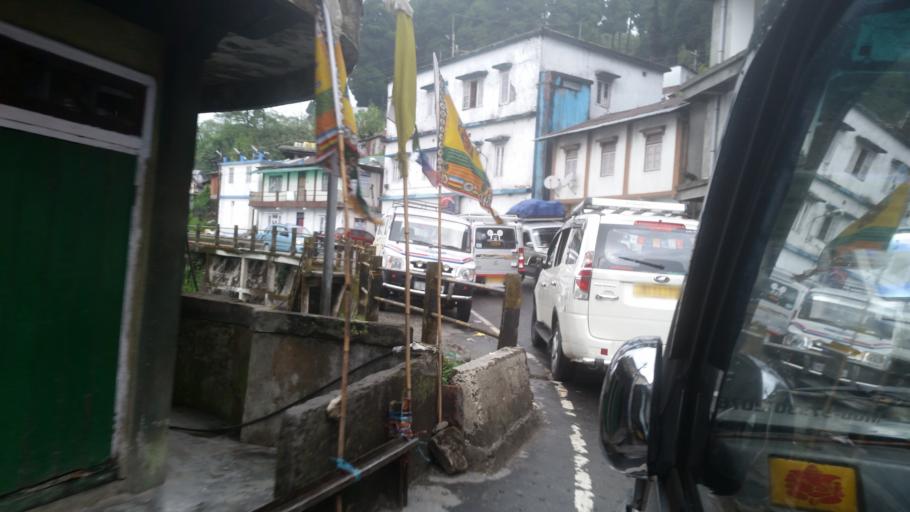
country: IN
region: West Bengal
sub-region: Darjiling
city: Darjiling
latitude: 27.0082
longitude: 88.2560
